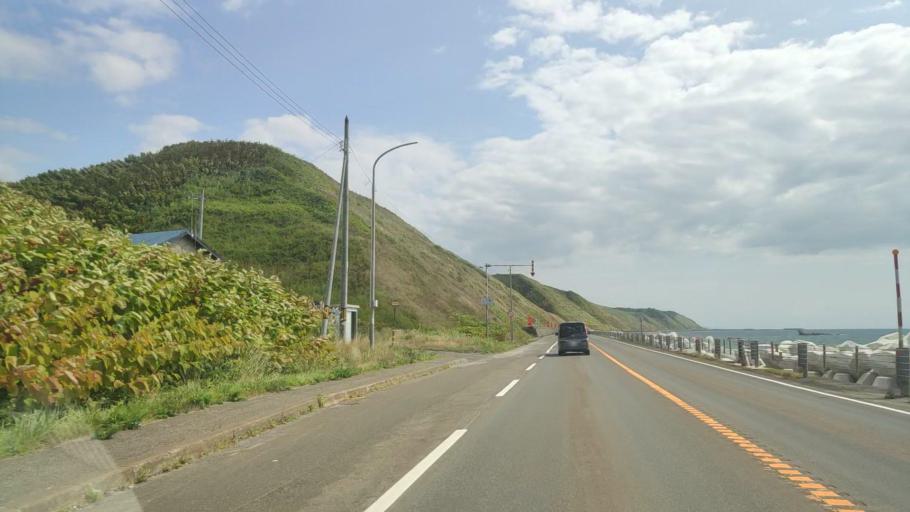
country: JP
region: Hokkaido
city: Rumoi
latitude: 44.2515
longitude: 141.6569
